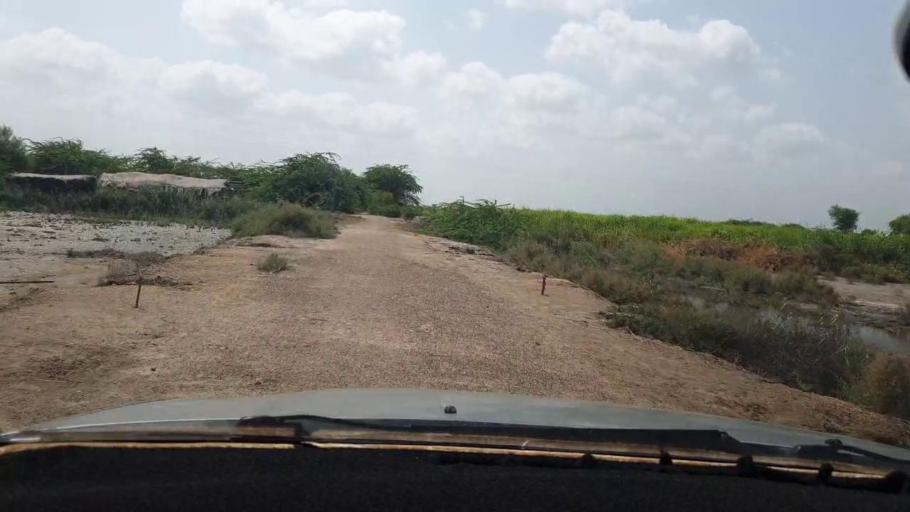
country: PK
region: Sindh
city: Tando Bago
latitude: 24.7499
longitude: 69.1532
